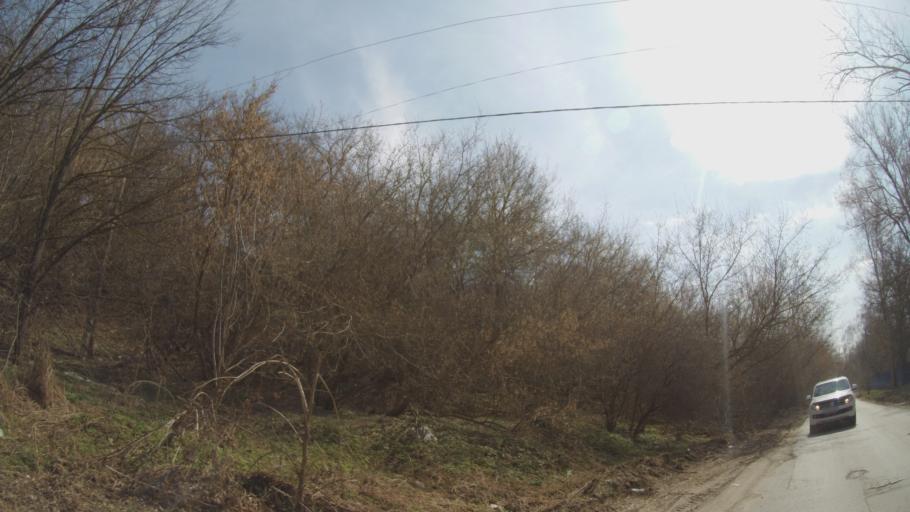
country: RU
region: Nizjnij Novgorod
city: Vyyezdnoye
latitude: 55.3879
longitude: 43.8101
